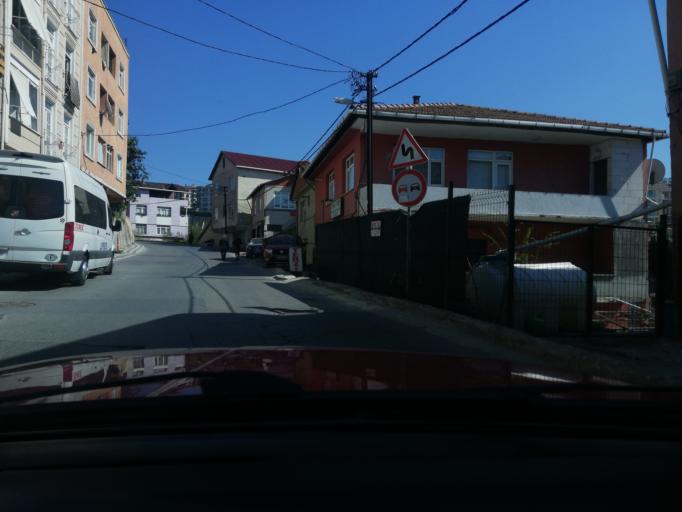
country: TR
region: Istanbul
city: Mahmut Sevket Pasa
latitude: 41.1138
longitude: 29.1119
